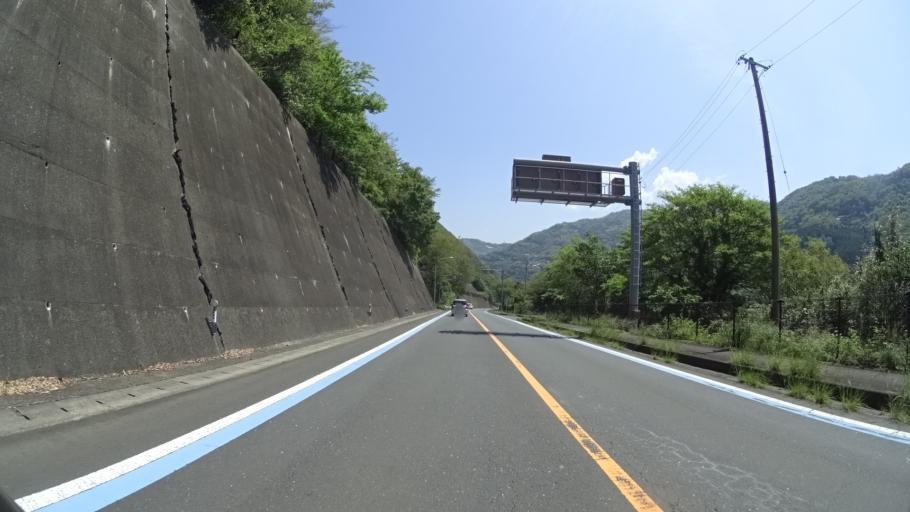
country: JP
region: Ehime
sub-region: Nishiuwa-gun
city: Ikata-cho
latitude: 33.4925
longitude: 132.3568
